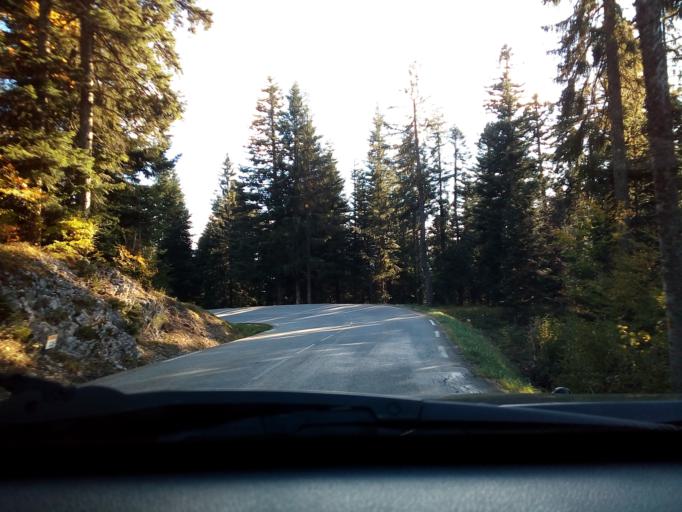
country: FR
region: Rhone-Alpes
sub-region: Departement de l'Isere
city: Le Sappey-en-Chartreuse
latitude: 45.2825
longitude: 5.7637
